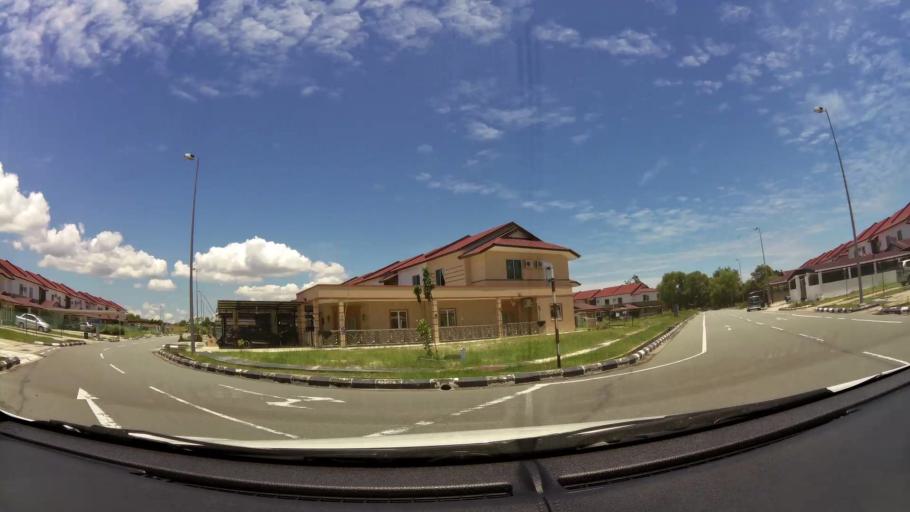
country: BN
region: Brunei and Muara
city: Bandar Seri Begawan
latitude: 5.0127
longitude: 115.0090
